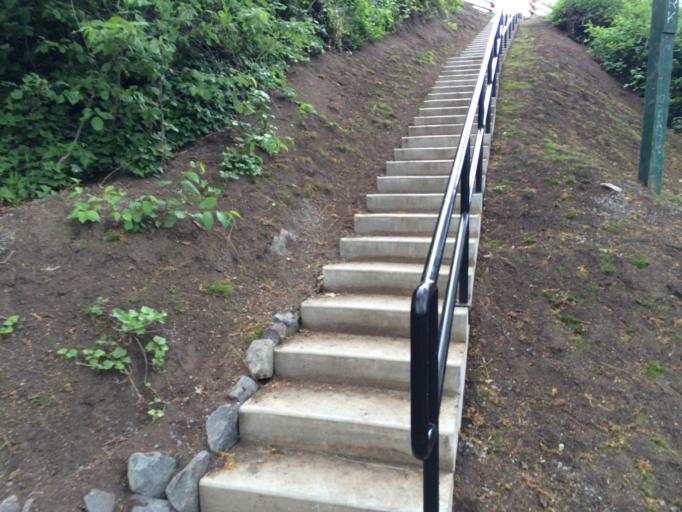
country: CA
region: British Columbia
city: Victoria
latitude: 48.4448
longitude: -123.3536
